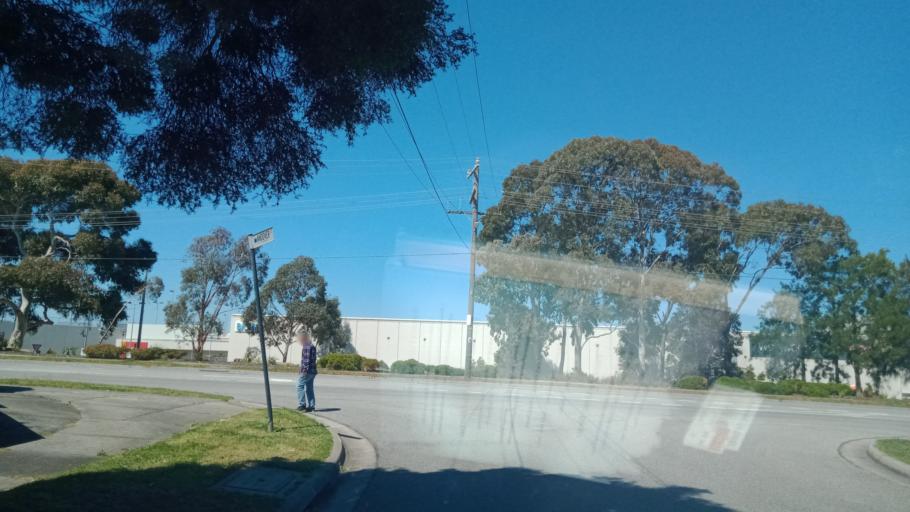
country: AU
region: Victoria
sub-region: Greater Dandenong
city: Noble Park North
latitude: -37.9353
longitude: 145.1875
